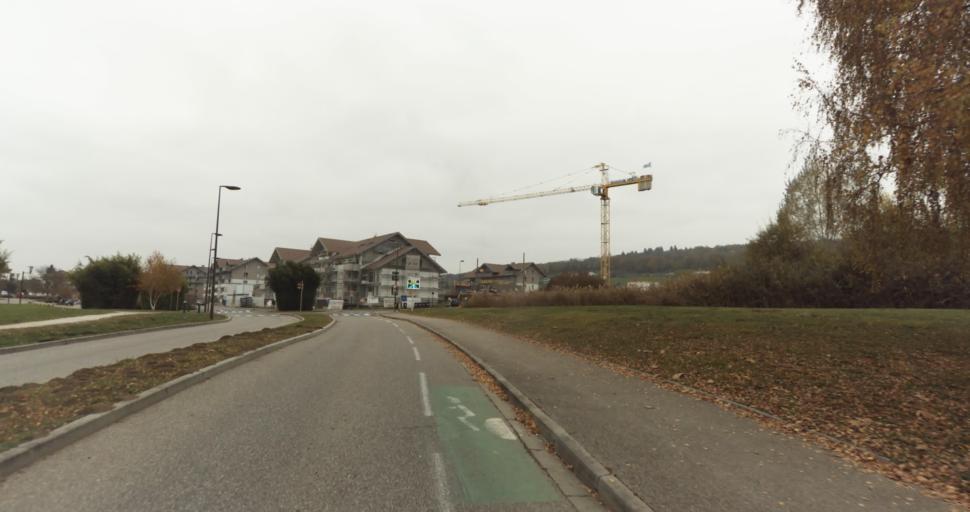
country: FR
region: Rhone-Alpes
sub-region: Departement de la Haute-Savoie
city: Poisy
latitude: 45.9267
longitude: 6.0621
